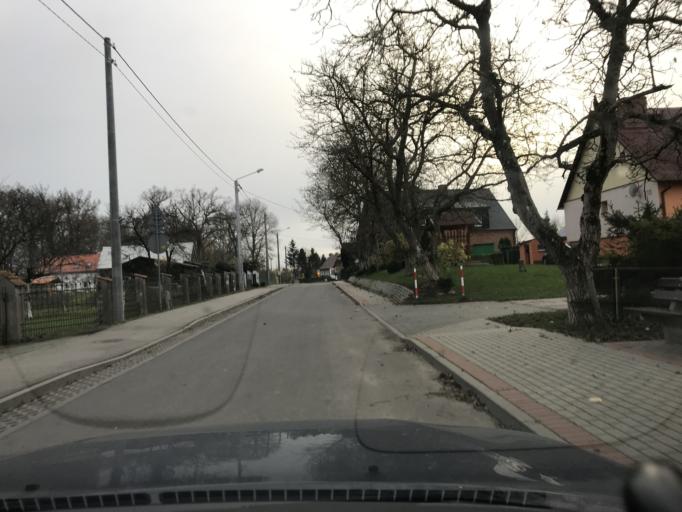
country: PL
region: Pomeranian Voivodeship
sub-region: Powiat slupski
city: Kobylnica
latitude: 54.4547
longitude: 16.8808
